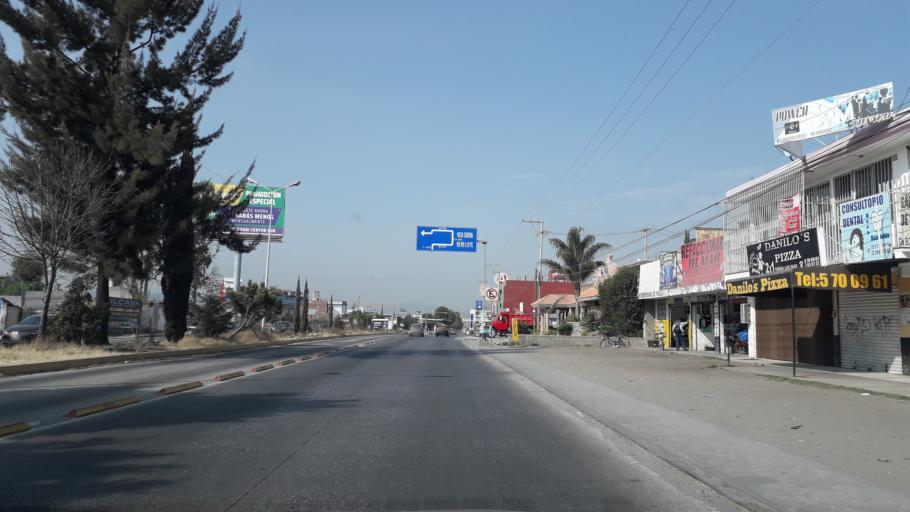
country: MX
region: Puebla
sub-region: Puebla
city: El Capulo (La Quebradora)
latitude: 18.9759
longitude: -98.2578
